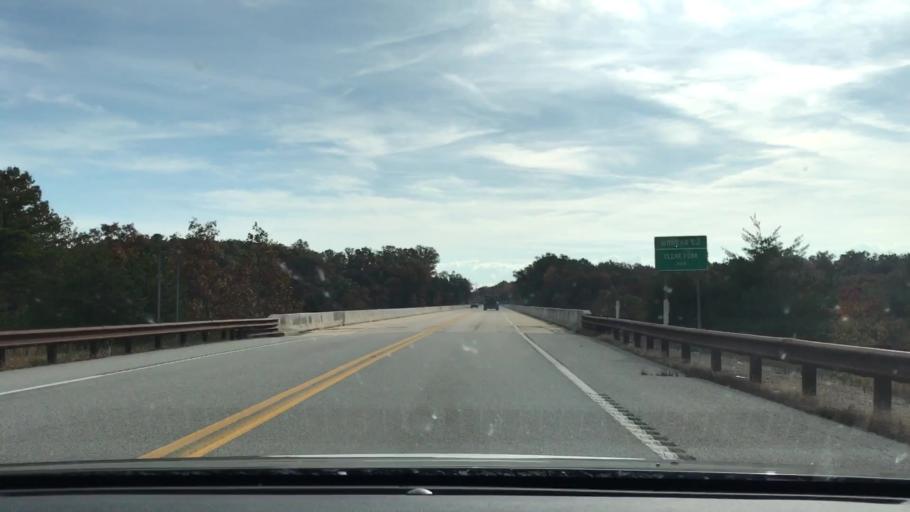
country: US
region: Tennessee
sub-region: Fentress County
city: Jamestown
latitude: 36.3528
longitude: -84.7293
